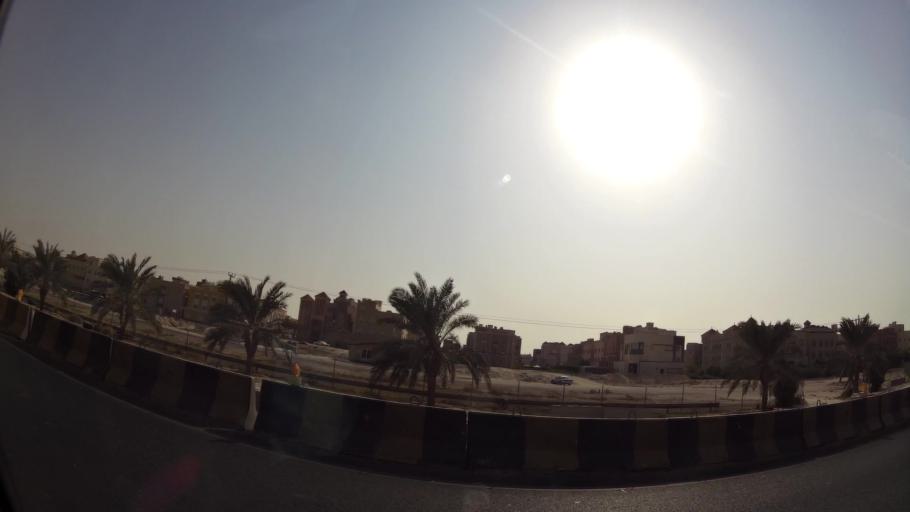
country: KW
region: Muhafazat al Jahra'
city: Al Jahra'
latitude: 29.3284
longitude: 47.7402
